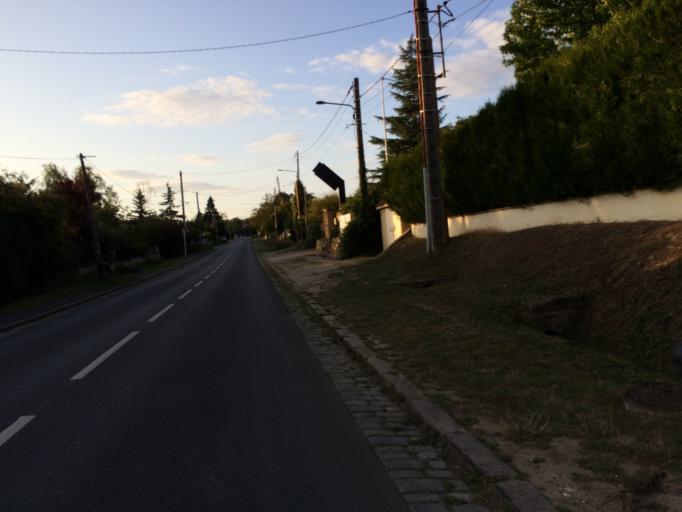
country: FR
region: Ile-de-France
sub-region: Departement de l'Essonne
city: Nozay
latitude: 48.6556
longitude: 2.2102
